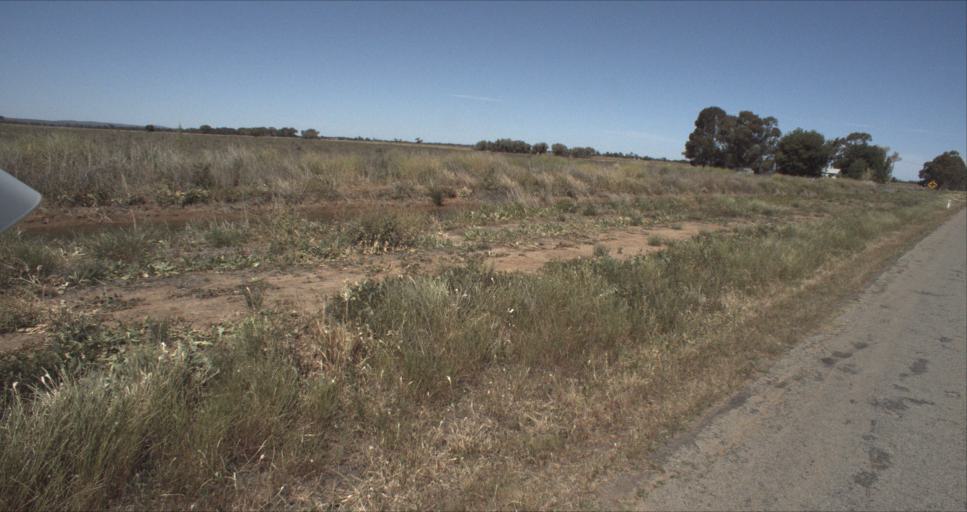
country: AU
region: New South Wales
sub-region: Leeton
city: Leeton
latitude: -34.5096
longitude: 146.3447
